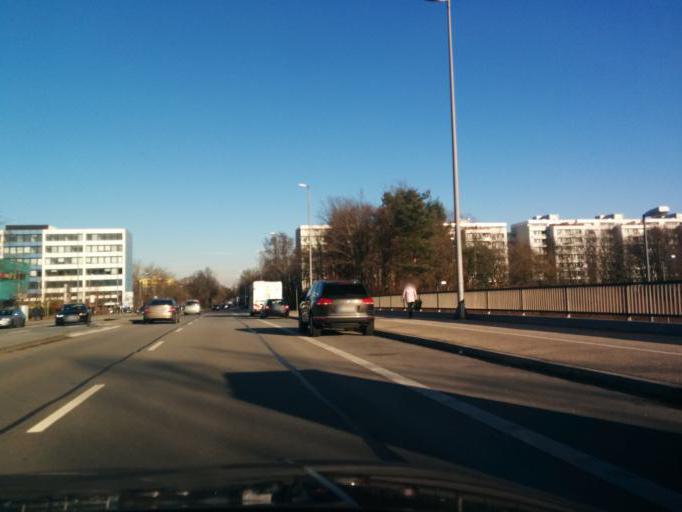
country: DE
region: Bavaria
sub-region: Upper Bavaria
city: Neubiberg
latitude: 48.1055
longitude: 11.6465
